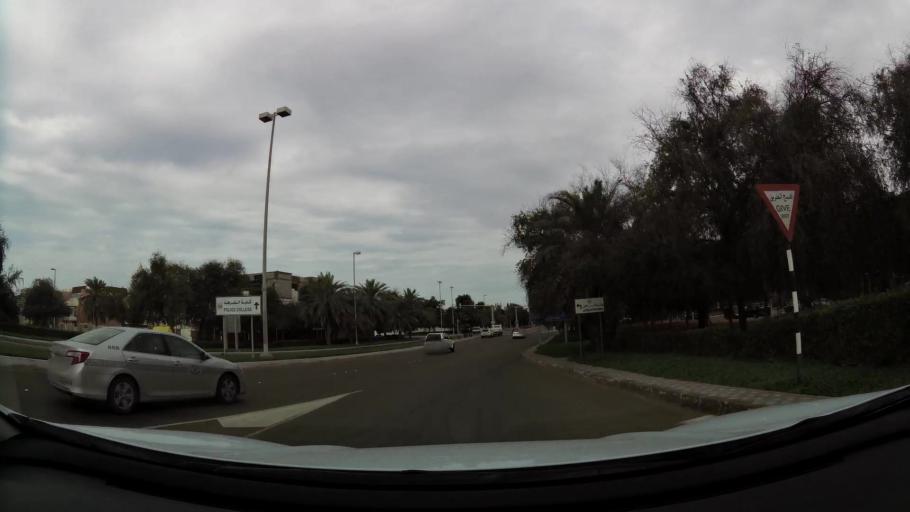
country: AE
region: Abu Dhabi
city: Abu Dhabi
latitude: 24.4242
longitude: 54.4176
